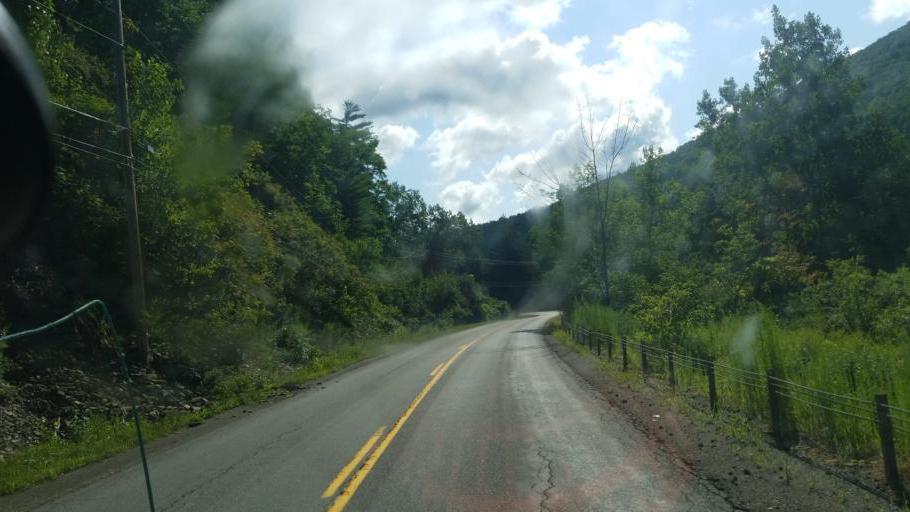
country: US
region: New York
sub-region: Steuben County
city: Canisteo
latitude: 42.2569
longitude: -77.6352
